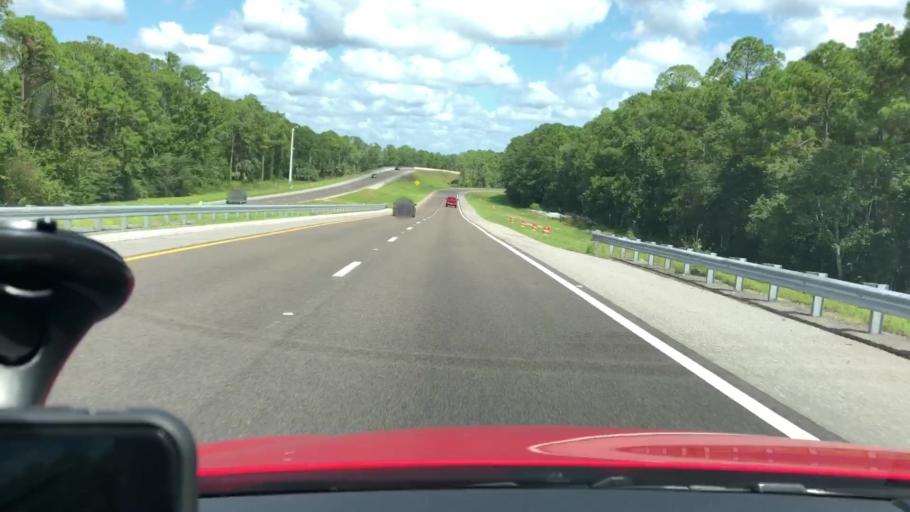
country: US
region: Florida
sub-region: Volusia County
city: Samsula-Spruce Creek
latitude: 29.1391
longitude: -81.1183
